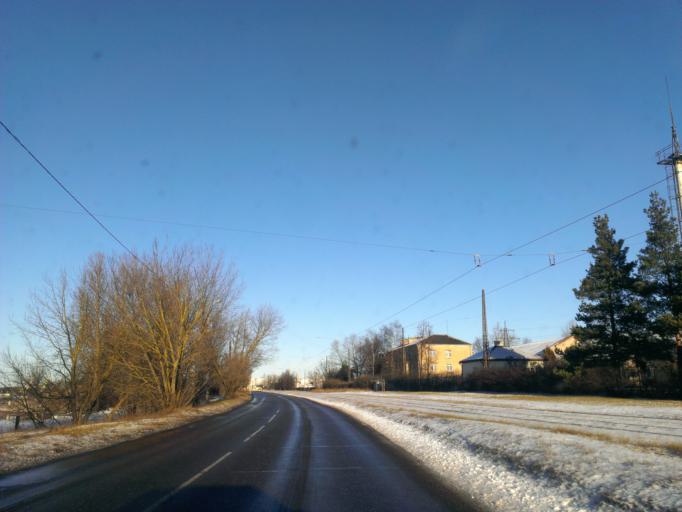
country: LV
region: Riga
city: Jaunciems
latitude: 57.0111
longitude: 24.1246
